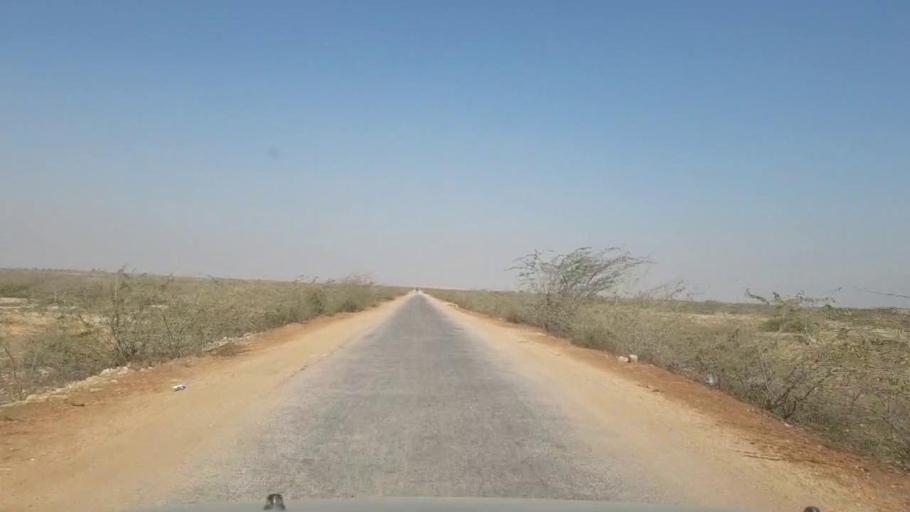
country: PK
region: Sindh
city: Thatta
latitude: 24.9398
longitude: 67.9509
